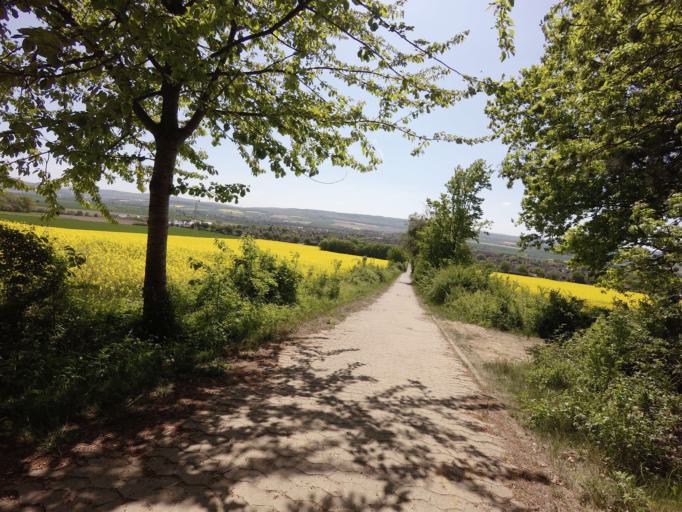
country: DE
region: Lower Saxony
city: Hildesheim
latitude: 52.1344
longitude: 9.9927
